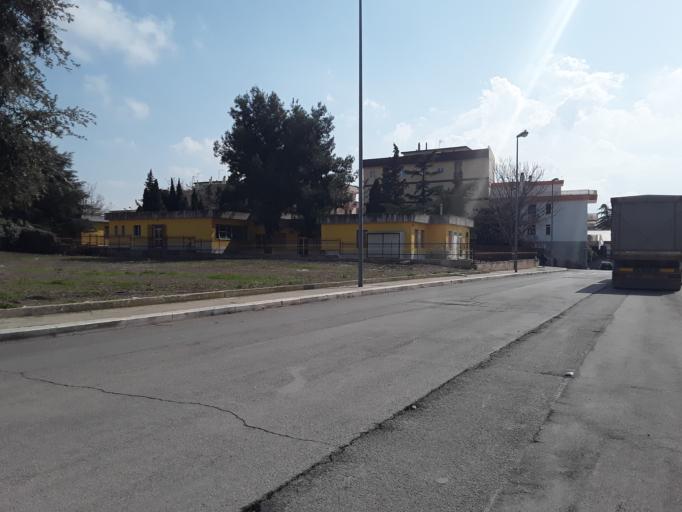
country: IT
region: Apulia
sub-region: Provincia di Bari
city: Ruvo di Puglia
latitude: 41.1215
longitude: 16.4807
